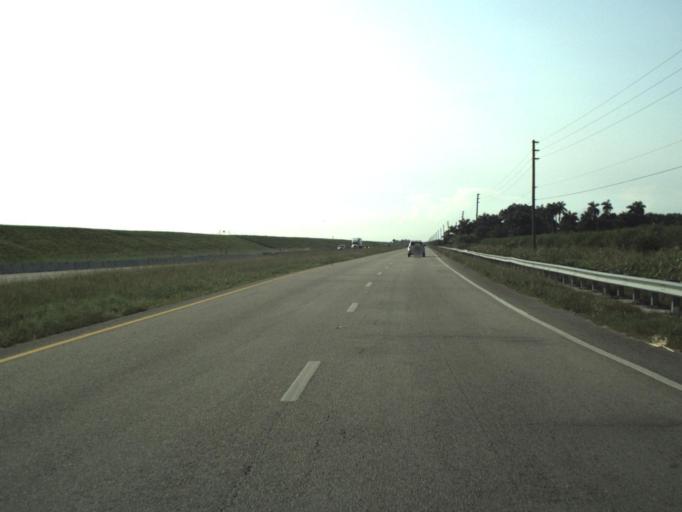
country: US
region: Florida
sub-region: Hendry County
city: Clewiston
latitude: 26.7241
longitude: -80.8482
